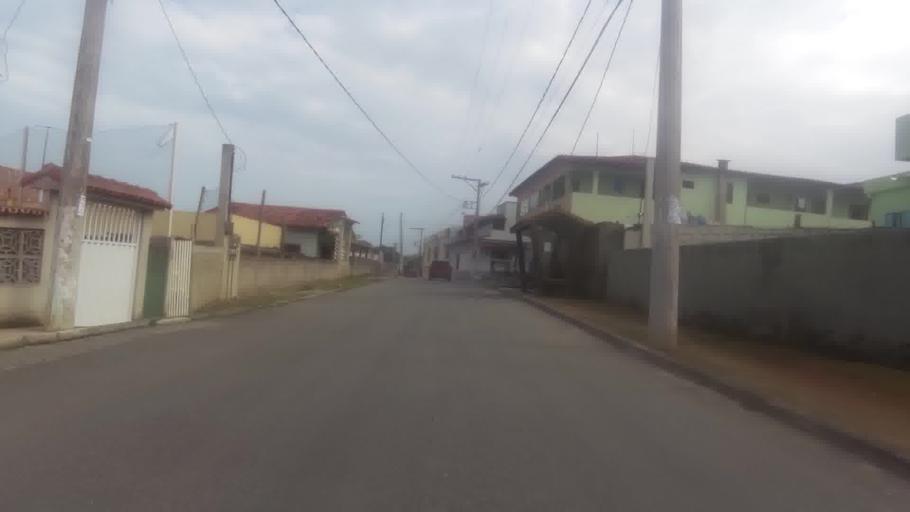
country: BR
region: Espirito Santo
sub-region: Guarapari
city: Guarapari
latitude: -20.7648
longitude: -40.5756
